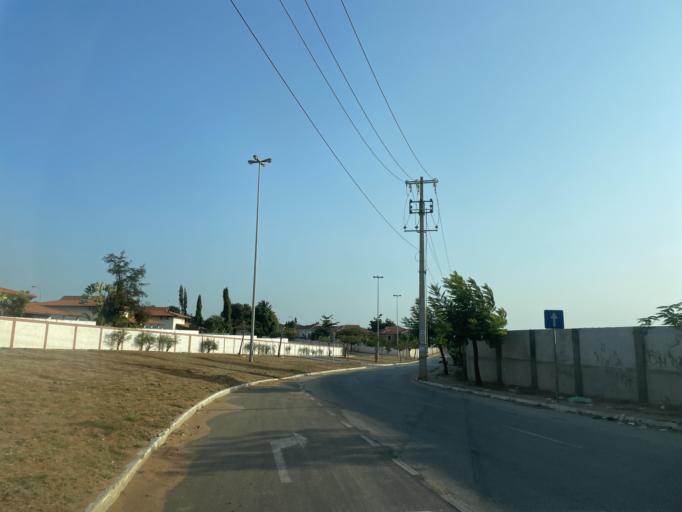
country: AO
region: Luanda
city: Luanda
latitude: -8.9244
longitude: 13.1793
